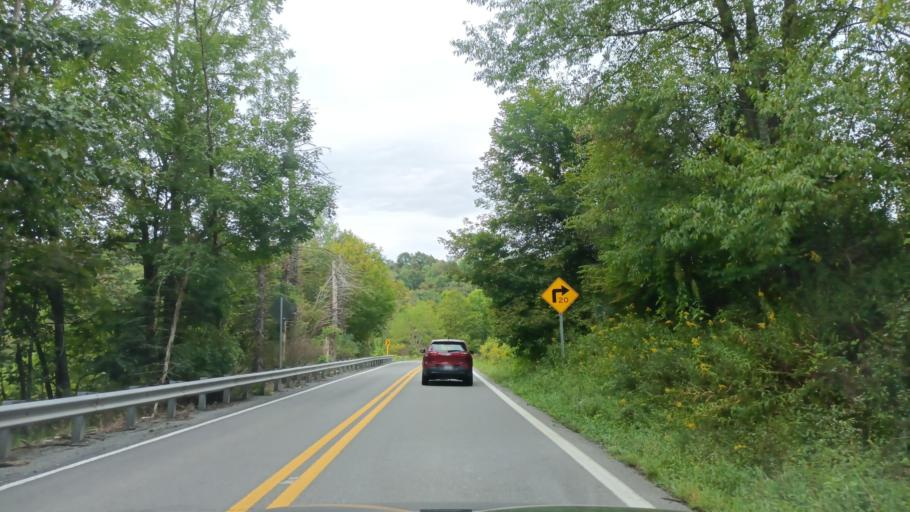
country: US
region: West Virginia
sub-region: Taylor County
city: Grafton
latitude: 39.3324
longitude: -79.8888
